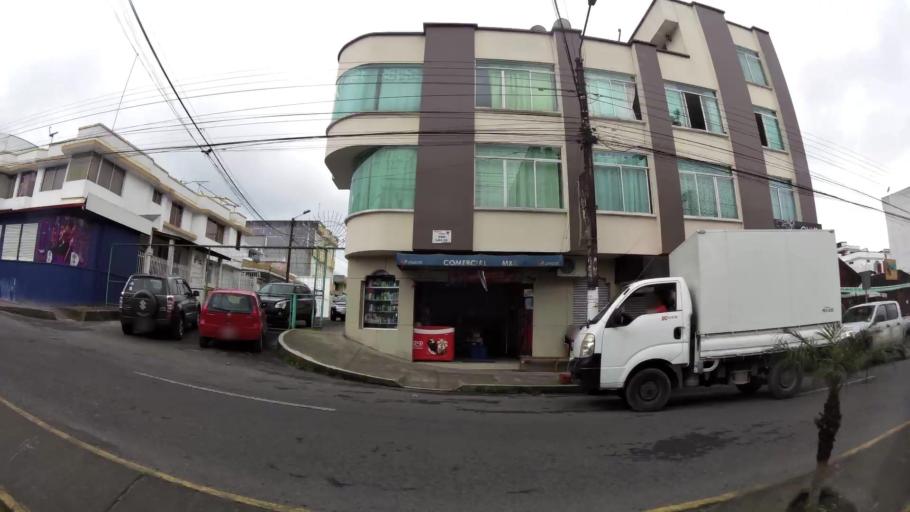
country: EC
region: Santo Domingo de los Tsachilas
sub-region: Canton Santo Domingo de los Colorados
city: Santo Domingo de los Colorados
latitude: -0.2497
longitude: -79.1523
